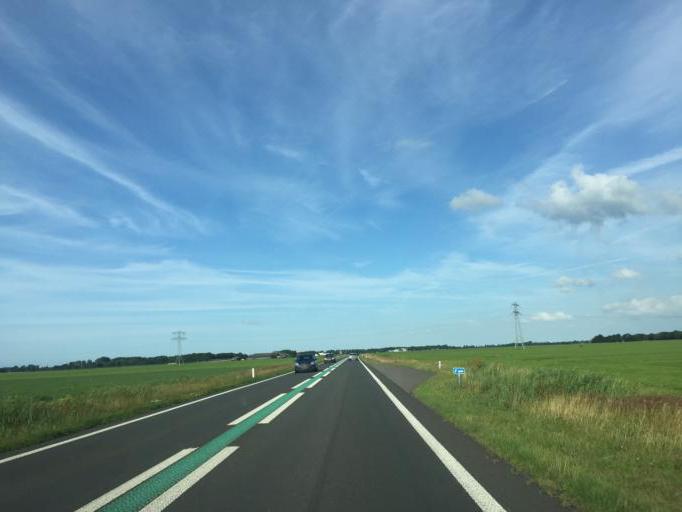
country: NL
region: Friesland
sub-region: Gemeente Dantumadiel
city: Rinsumageast
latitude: 53.3043
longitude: 5.9578
